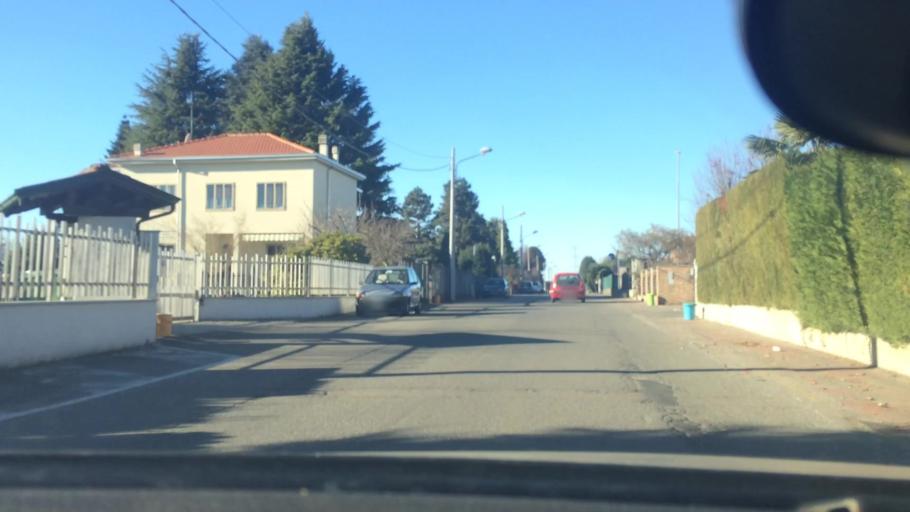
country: IT
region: Lombardy
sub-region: Provincia di Monza e Brianza
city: Ceriano Laghetto
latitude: 45.6264
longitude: 9.0755
